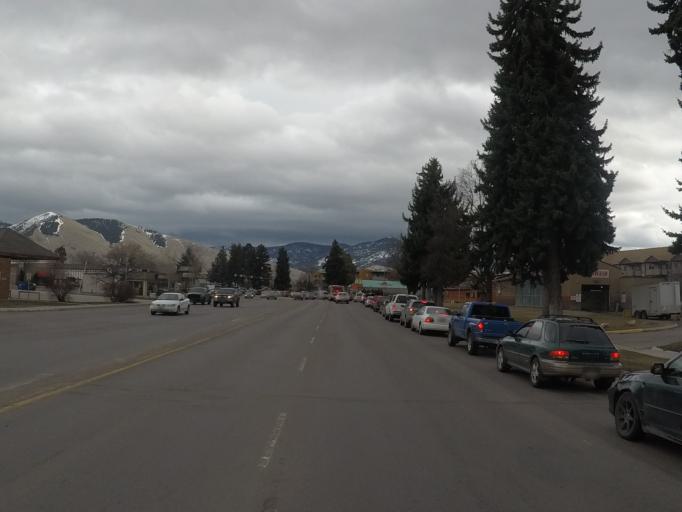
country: US
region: Montana
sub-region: Missoula County
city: Missoula
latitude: 46.8798
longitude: -114.0212
